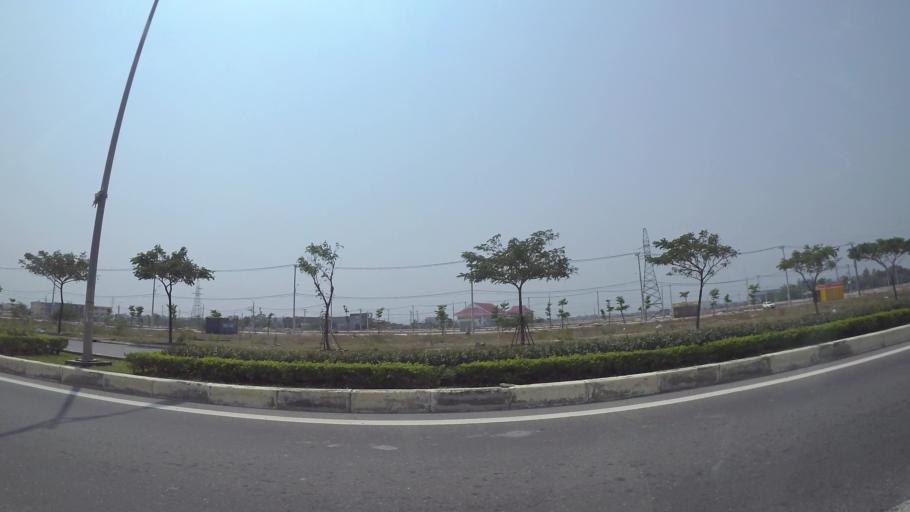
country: VN
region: Da Nang
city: Ngu Hanh Son
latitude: 15.9955
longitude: 108.2351
